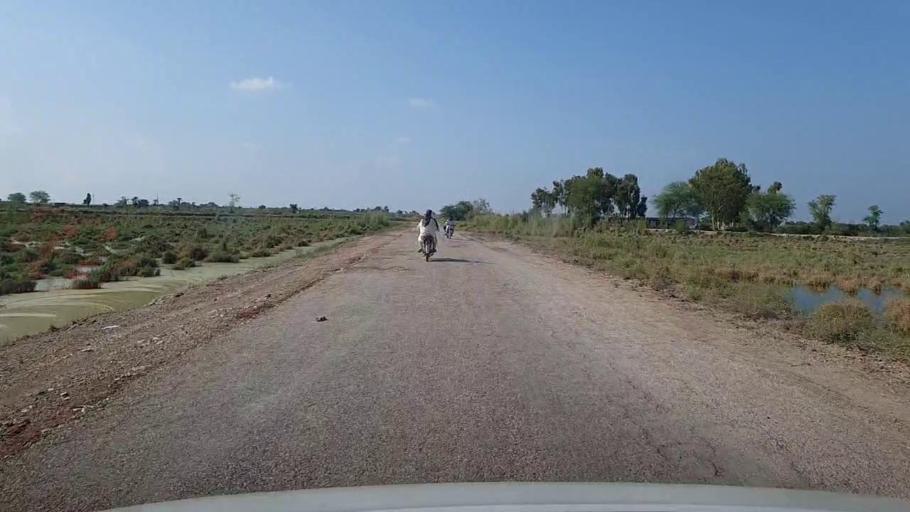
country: PK
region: Sindh
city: Kandiaro
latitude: 27.0637
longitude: 68.3156
